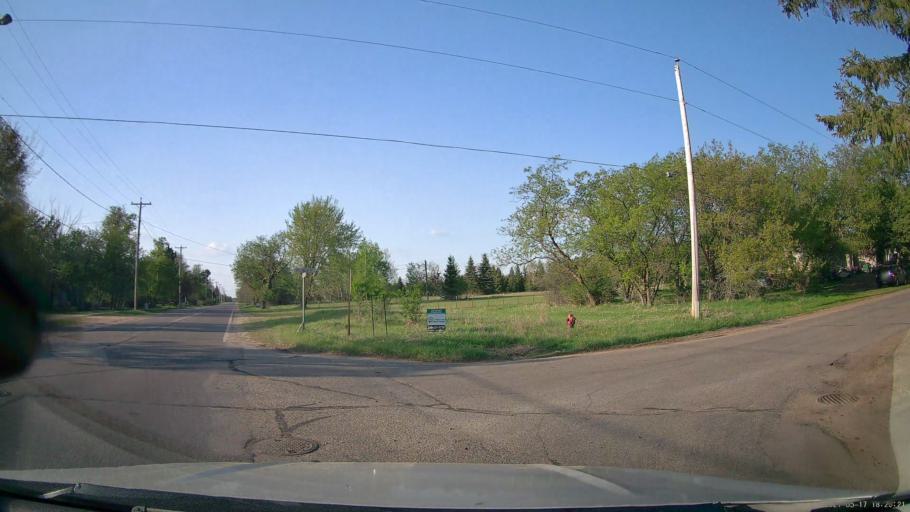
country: US
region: Minnesota
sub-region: Hubbard County
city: Park Rapids
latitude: 46.9253
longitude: -95.0476
